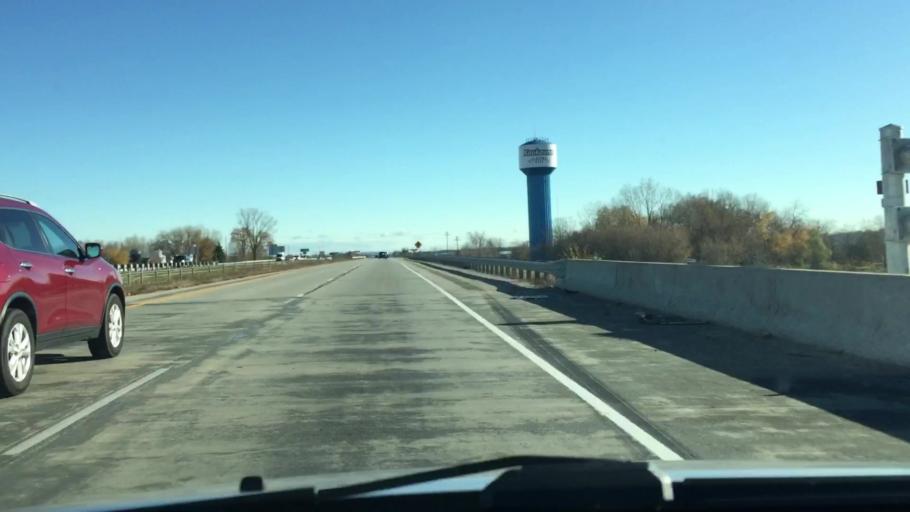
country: US
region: Wisconsin
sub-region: Outagamie County
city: Kaukauna
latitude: 44.2994
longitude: -88.2720
